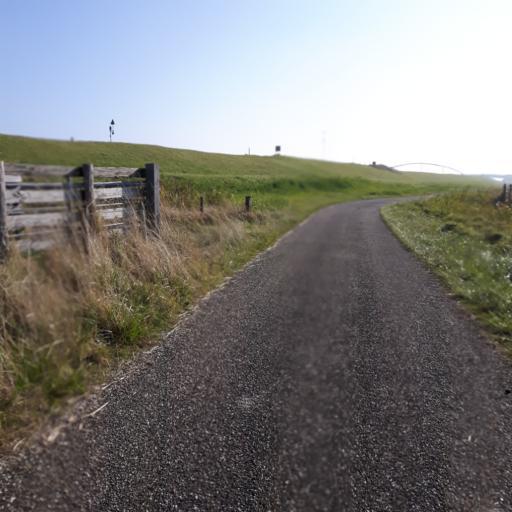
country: NL
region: Zeeland
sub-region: Gemeente Reimerswaal
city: Yerseke
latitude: 51.4765
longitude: 4.0030
